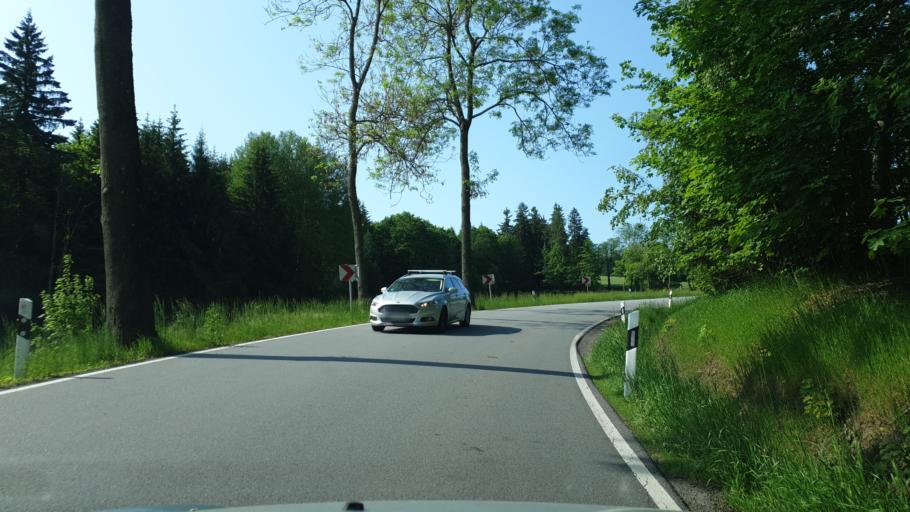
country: DE
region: Saxony
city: Zschorlau
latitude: 50.5492
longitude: 12.6233
